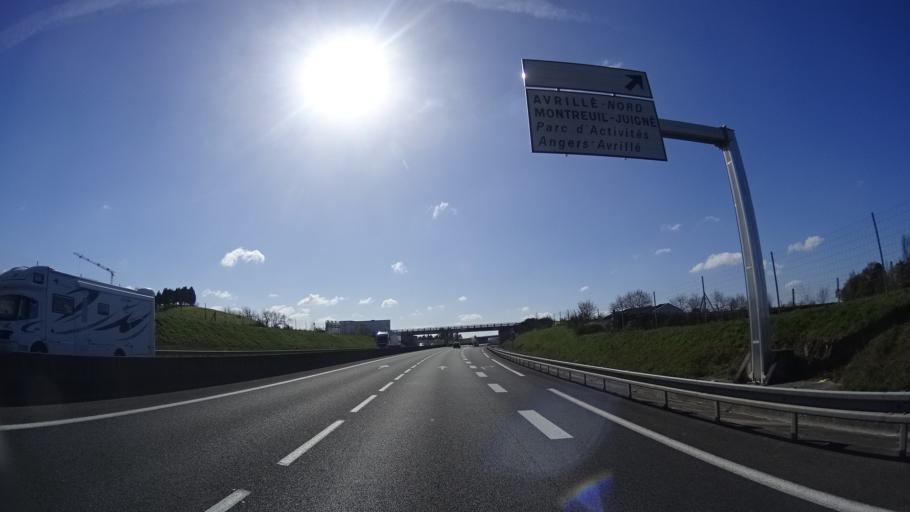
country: FR
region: Pays de la Loire
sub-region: Departement de Maine-et-Loire
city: Avrille
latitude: 47.5183
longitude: -0.6207
